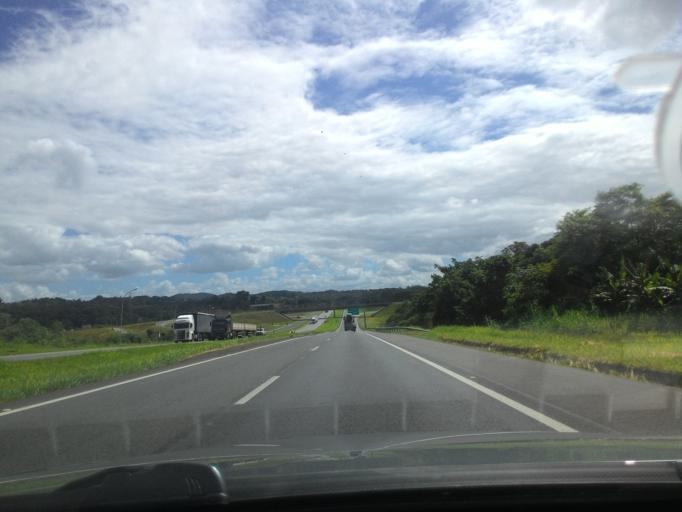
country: BR
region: Sao Paulo
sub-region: Pariquera-Acu
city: Pariquera Acu
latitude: -24.6414
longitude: -47.9157
